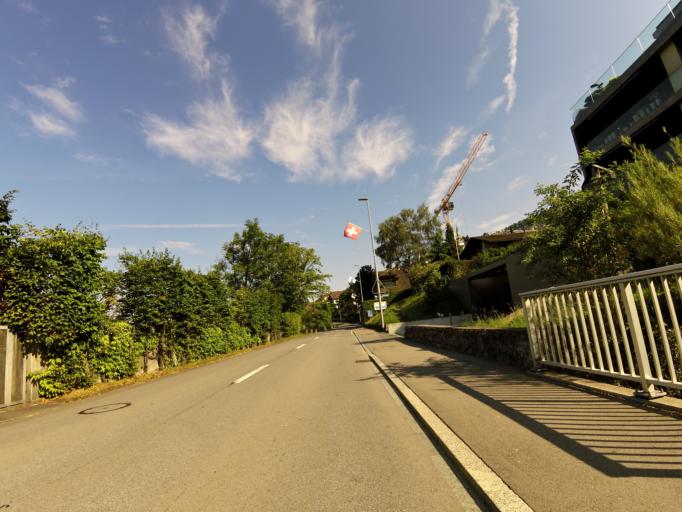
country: CH
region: Zug
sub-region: Zug
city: Walchwil
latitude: 47.0975
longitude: 8.5152
